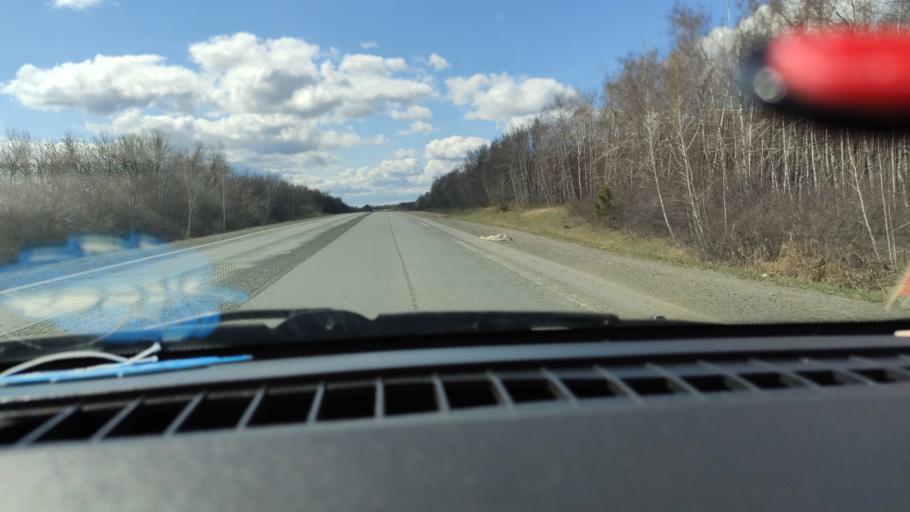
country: RU
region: Saratov
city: Dukhovnitskoye
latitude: 52.6317
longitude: 48.1846
